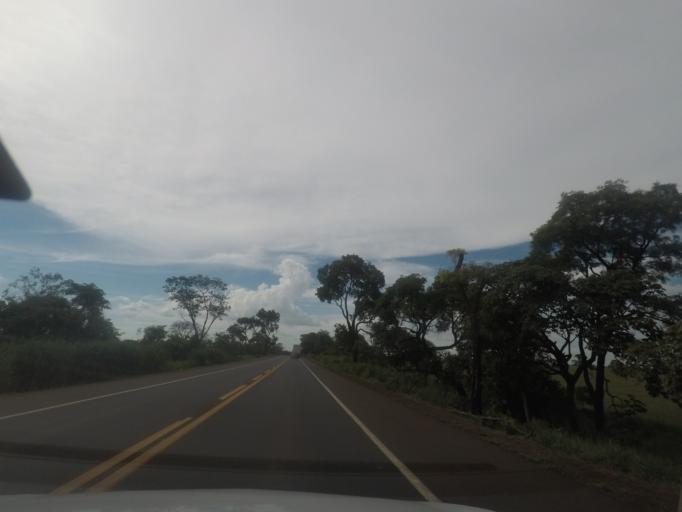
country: BR
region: Minas Gerais
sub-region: Prata
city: Prata
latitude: -19.2493
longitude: -48.9266
